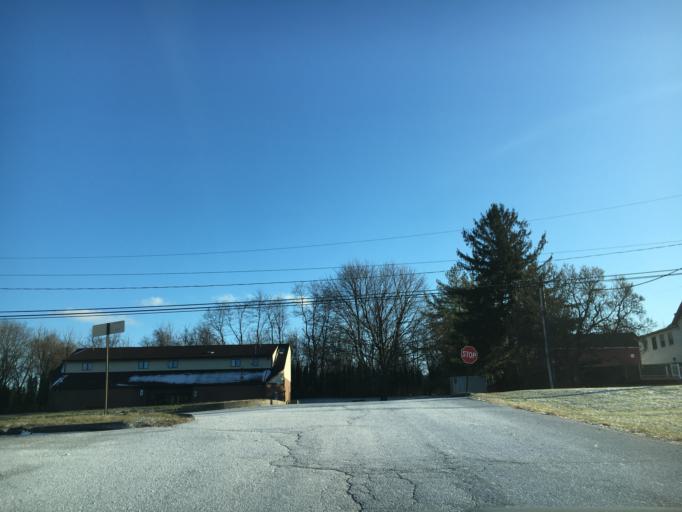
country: US
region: Pennsylvania
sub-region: Lehigh County
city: Hokendauqua
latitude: 40.6512
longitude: -75.4934
